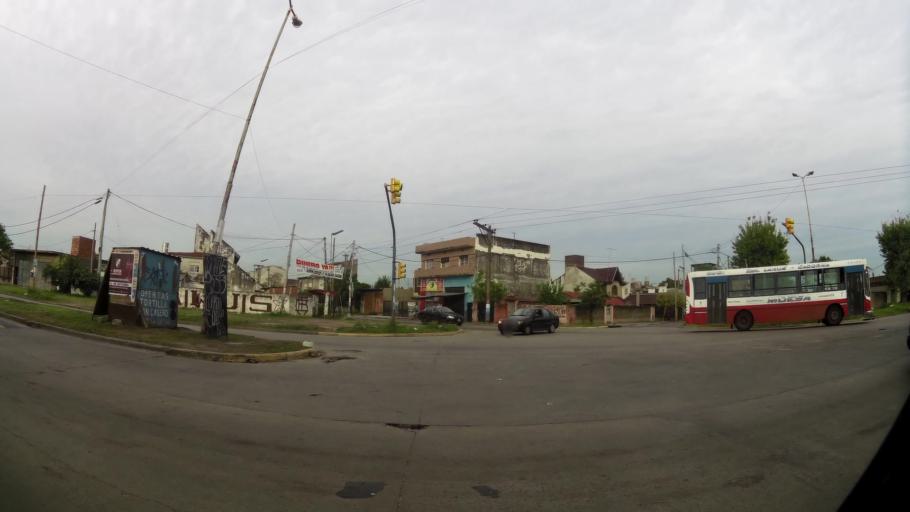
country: AR
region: Buenos Aires
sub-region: Partido de Lanus
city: Lanus
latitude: -34.7338
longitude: -58.3451
